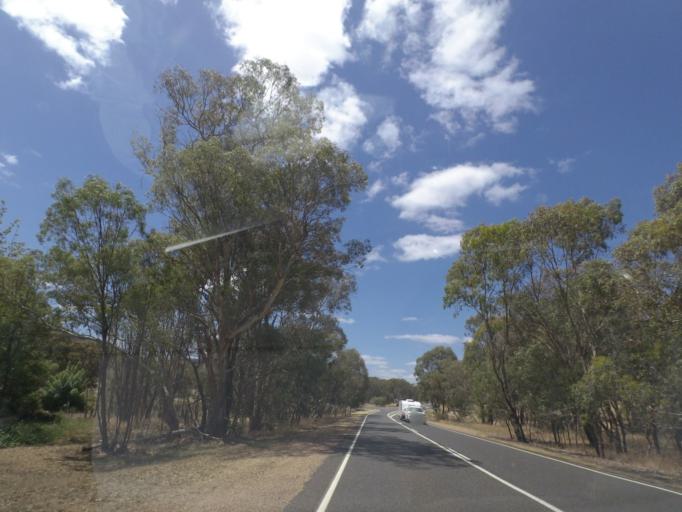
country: AU
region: Victoria
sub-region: Wangaratta
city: Wangaratta
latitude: -36.4649
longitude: 146.2150
